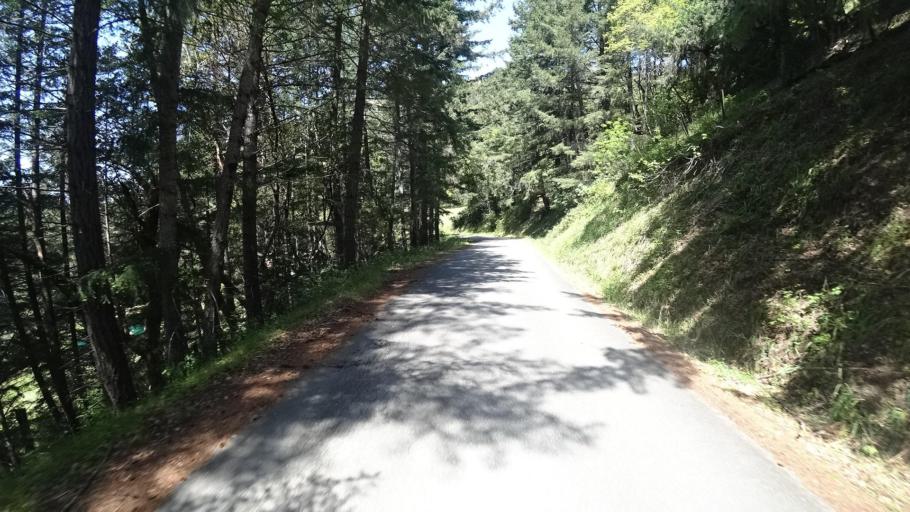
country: US
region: California
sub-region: Humboldt County
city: Redway
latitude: 40.1911
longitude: -123.5352
